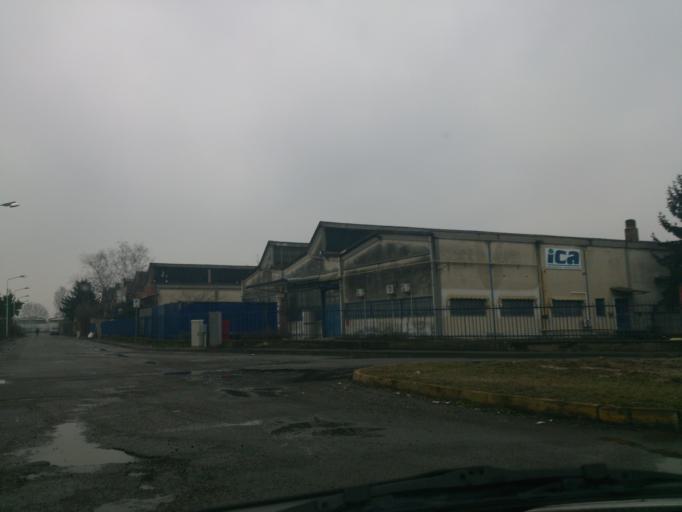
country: IT
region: Lombardy
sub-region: Citta metropolitana di Milano
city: Civesio
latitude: 45.4001
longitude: 9.2653
